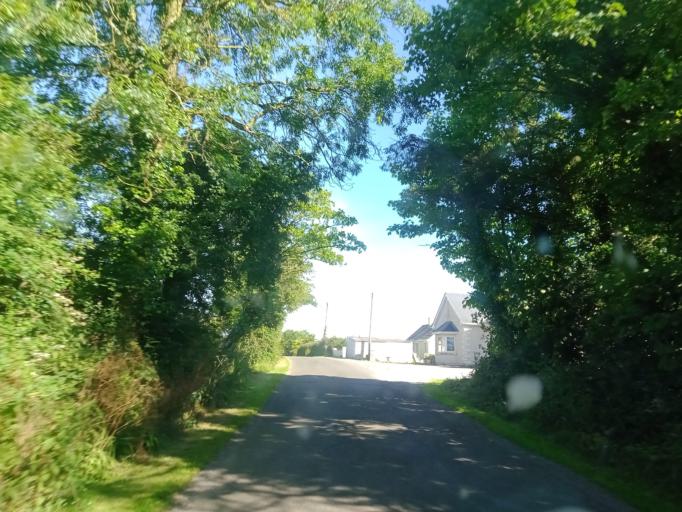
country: IE
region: Leinster
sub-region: Kilkenny
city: Ballyragget
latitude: 52.7817
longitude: -7.4177
